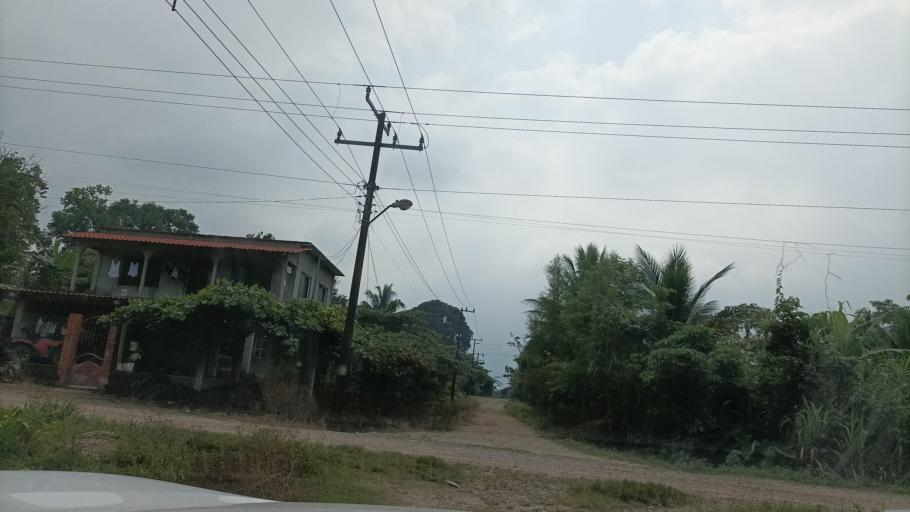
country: MX
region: Veracruz
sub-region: Uxpanapa
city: Poblado 10
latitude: 17.5422
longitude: -94.2377
